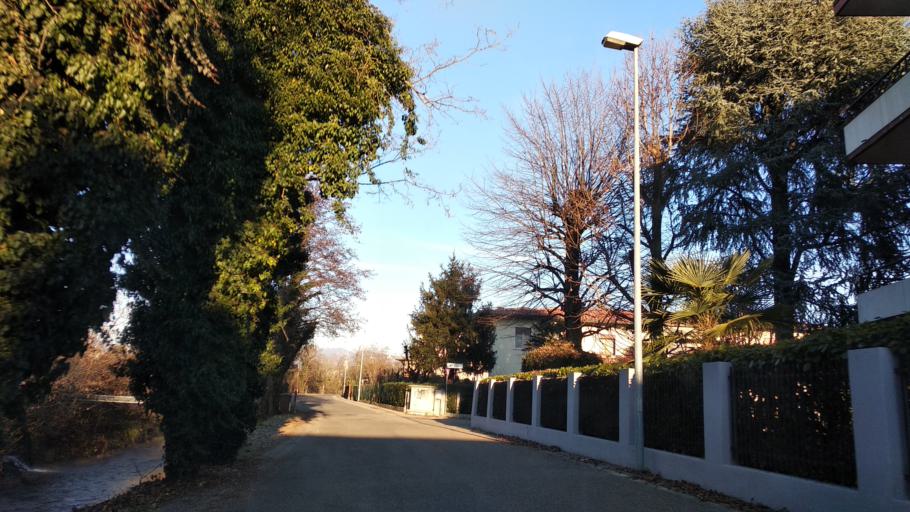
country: IT
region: Veneto
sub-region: Provincia di Vicenza
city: Crispi Cavour
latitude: 45.5886
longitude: 11.5272
